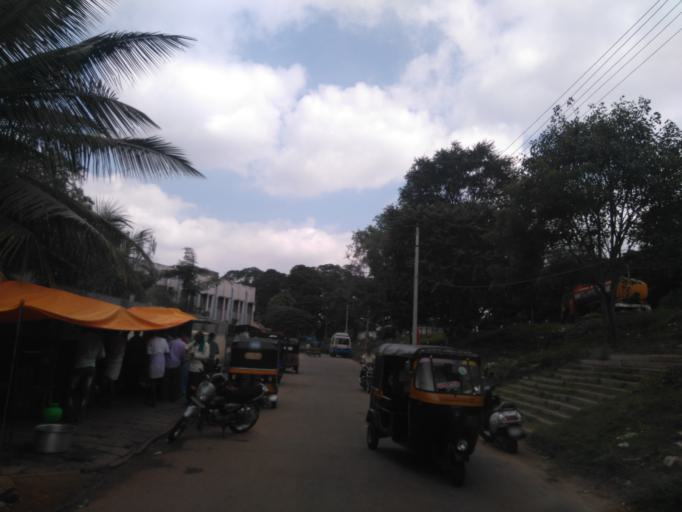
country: IN
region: Karnataka
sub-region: Mysore
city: Mysore
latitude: 12.3000
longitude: 76.6567
